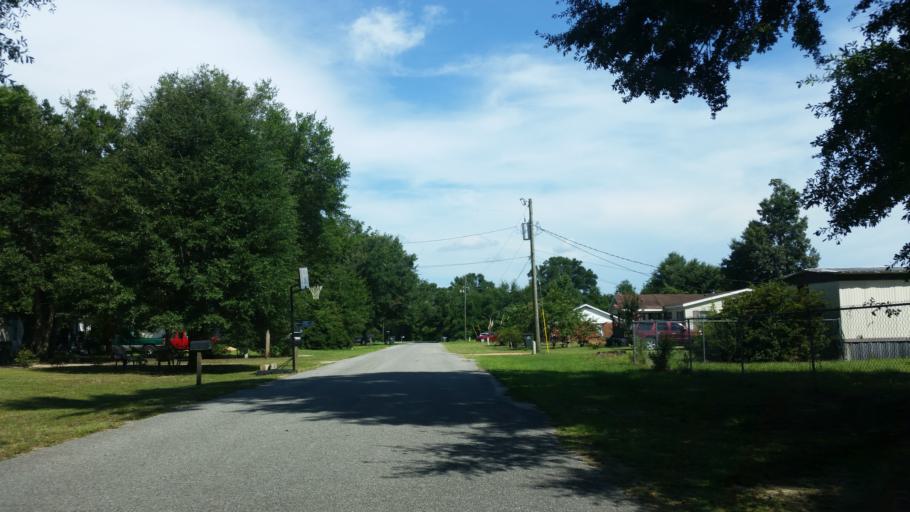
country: US
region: Florida
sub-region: Santa Rosa County
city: Pace
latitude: 30.5944
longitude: -87.1465
